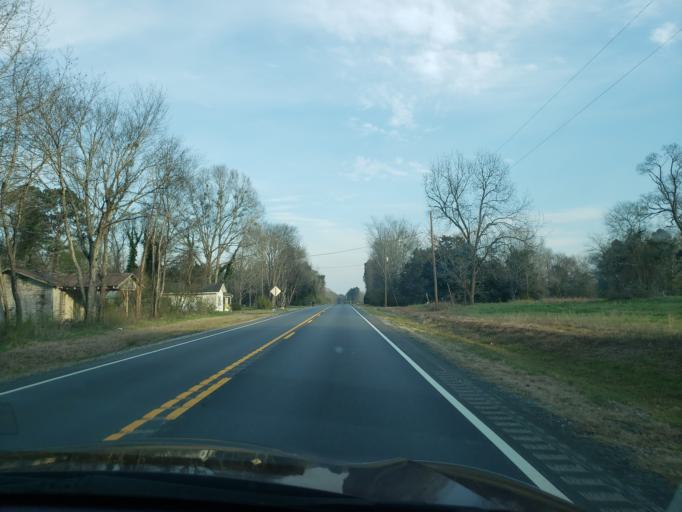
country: US
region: Alabama
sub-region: Hale County
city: Moundville
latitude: 32.8947
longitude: -87.6194
